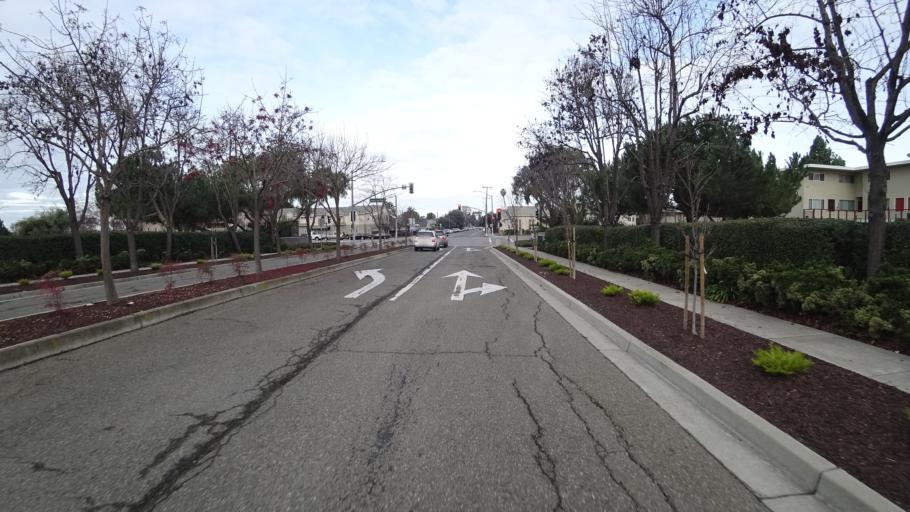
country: US
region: California
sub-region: Alameda County
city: Union City
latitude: 37.6276
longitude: -122.0485
